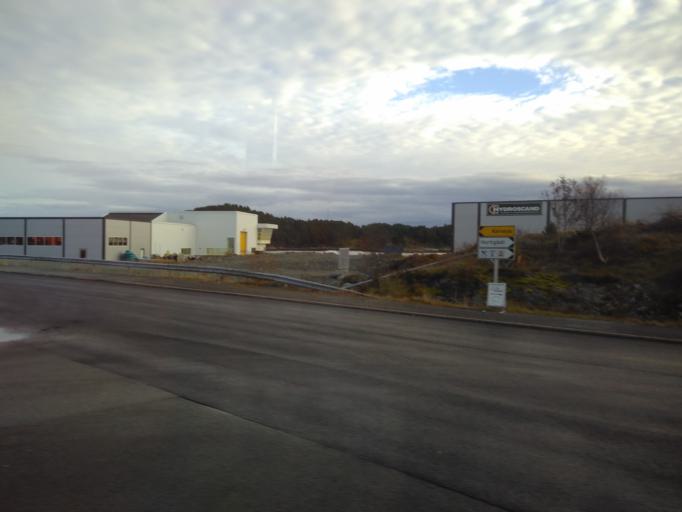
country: NO
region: Sor-Trondelag
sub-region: Hitra
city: Fillan
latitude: 63.5190
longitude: 9.1108
